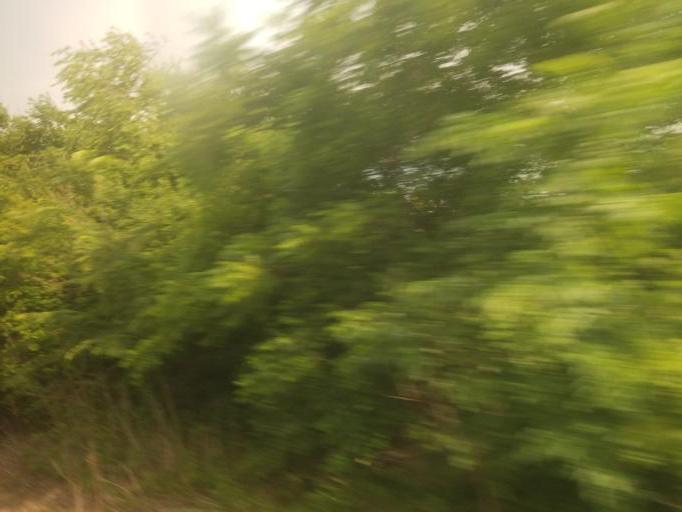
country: US
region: Illinois
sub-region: Bureau County
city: Princeton
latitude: 41.3434
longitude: -89.6371
